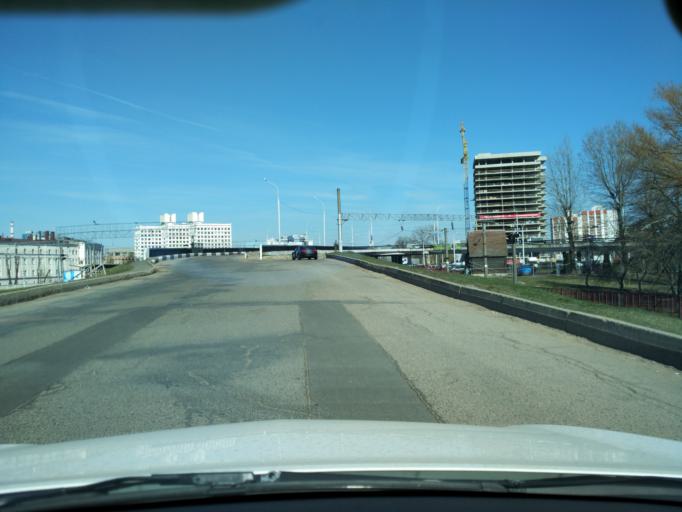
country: BY
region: Minsk
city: Minsk
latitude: 53.8827
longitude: 27.5340
